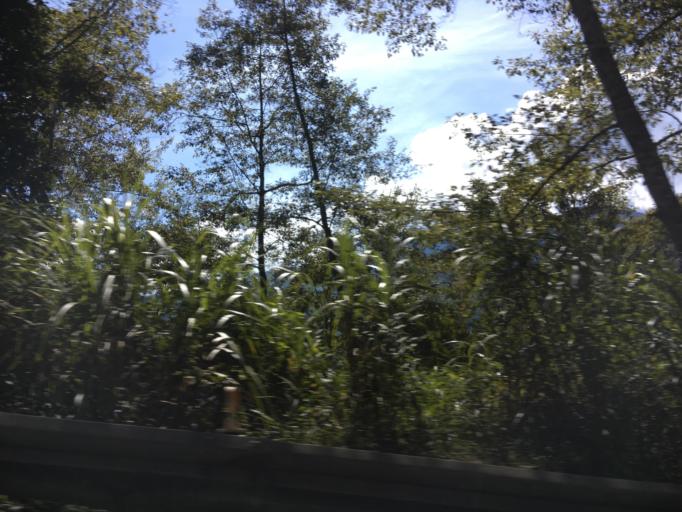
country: TW
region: Taiwan
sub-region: Yilan
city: Yilan
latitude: 24.5280
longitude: 121.5202
